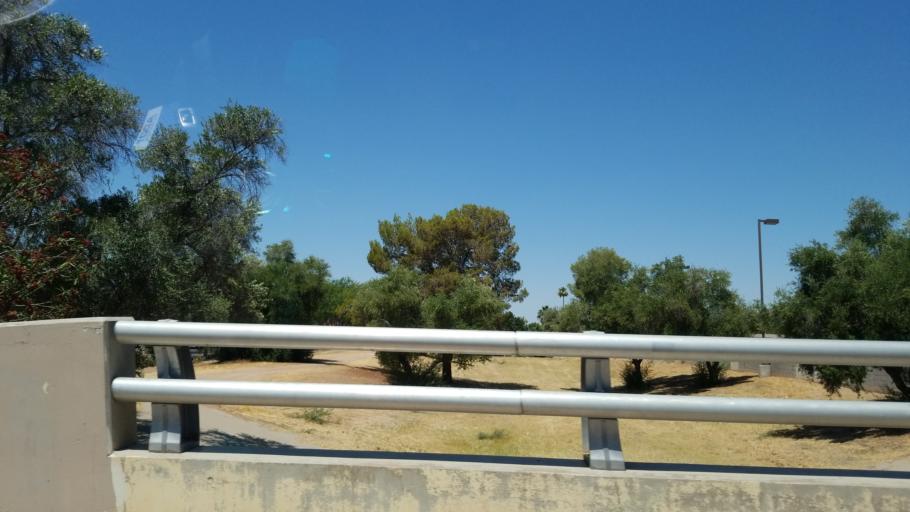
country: US
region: Arizona
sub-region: Maricopa County
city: Glendale
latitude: 33.6327
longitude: -112.1192
